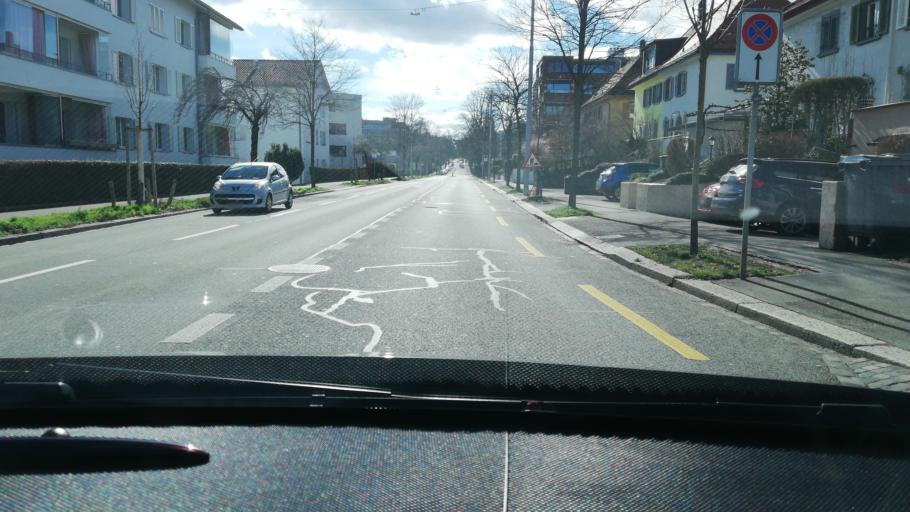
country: CH
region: Zurich
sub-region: Bezirk Zuerich
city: Zuerich (Kreis 6) / Unterstrass
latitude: 47.4021
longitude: 8.5358
